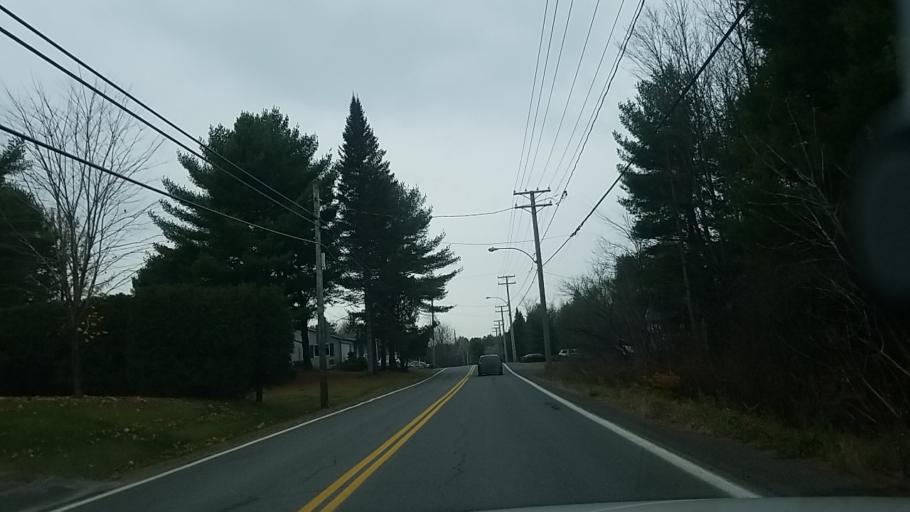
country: CA
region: Quebec
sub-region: Laurentides
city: Saint-Colomban
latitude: 45.7849
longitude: -74.0863
